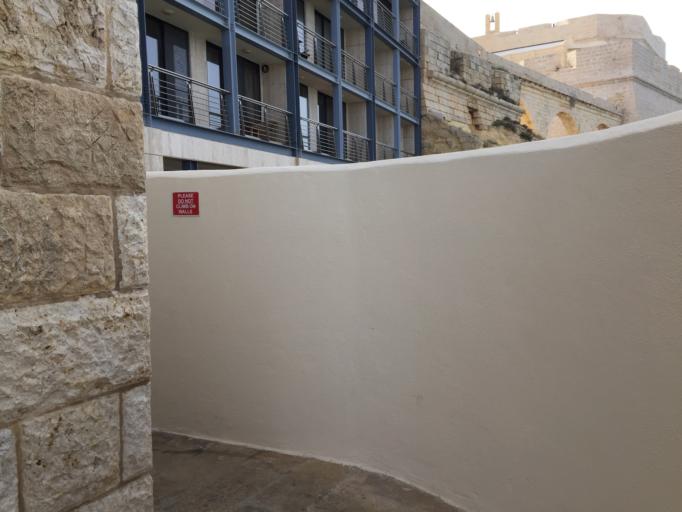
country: MT
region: Il-Birgu
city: Vittoriosa
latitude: 35.8908
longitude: 14.5202
